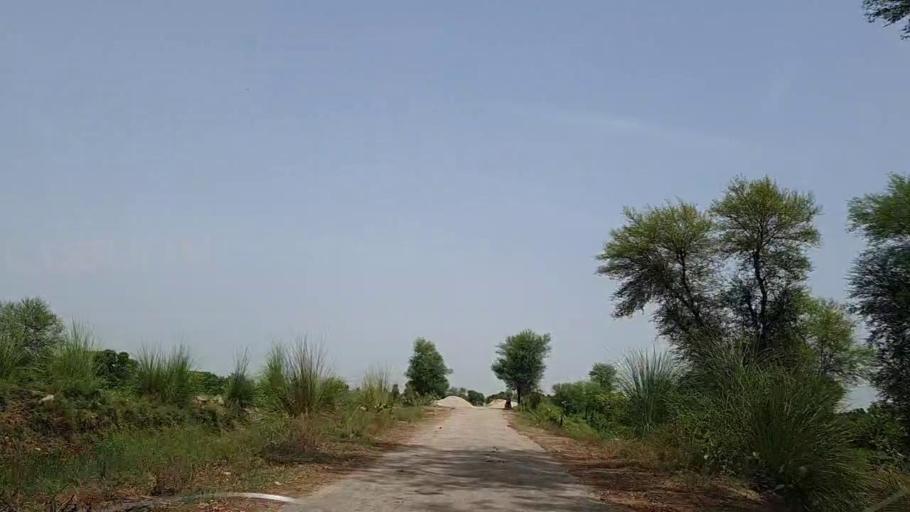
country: PK
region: Sindh
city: Tharu Shah
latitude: 26.9431
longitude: 68.0250
